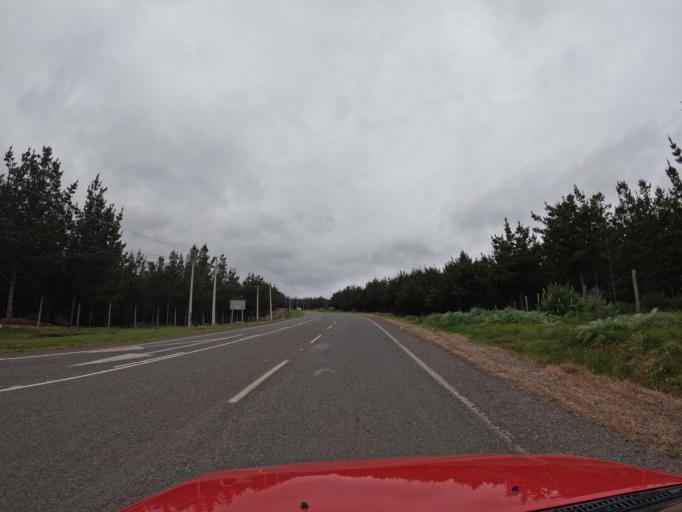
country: CL
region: O'Higgins
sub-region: Provincia de Colchagua
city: Santa Cruz
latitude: -34.6348
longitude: -72.0338
